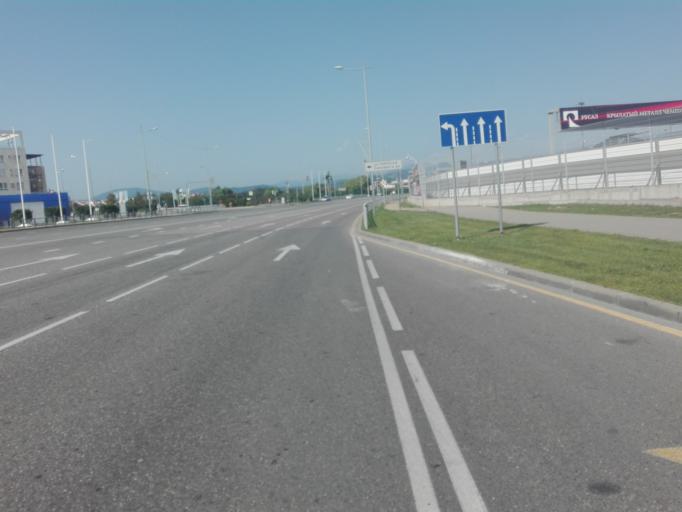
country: RU
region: Krasnodarskiy
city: Adler
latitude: 43.4038
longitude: 39.9471
